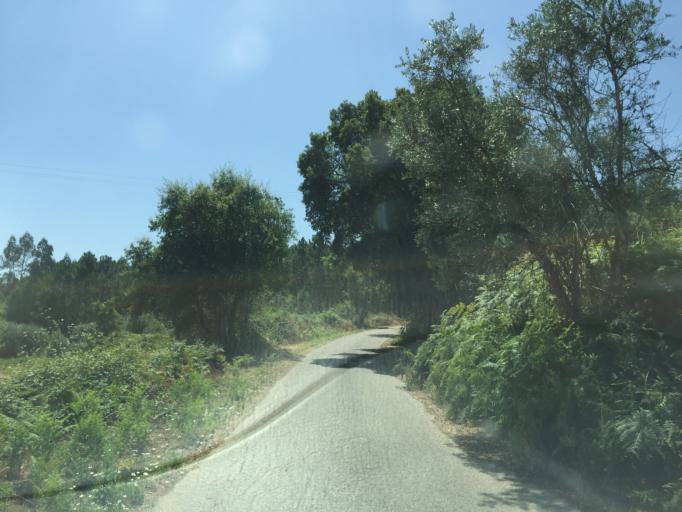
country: PT
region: Santarem
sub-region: Ferreira do Zezere
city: Ferreira do Zezere
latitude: 39.6519
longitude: -8.3024
